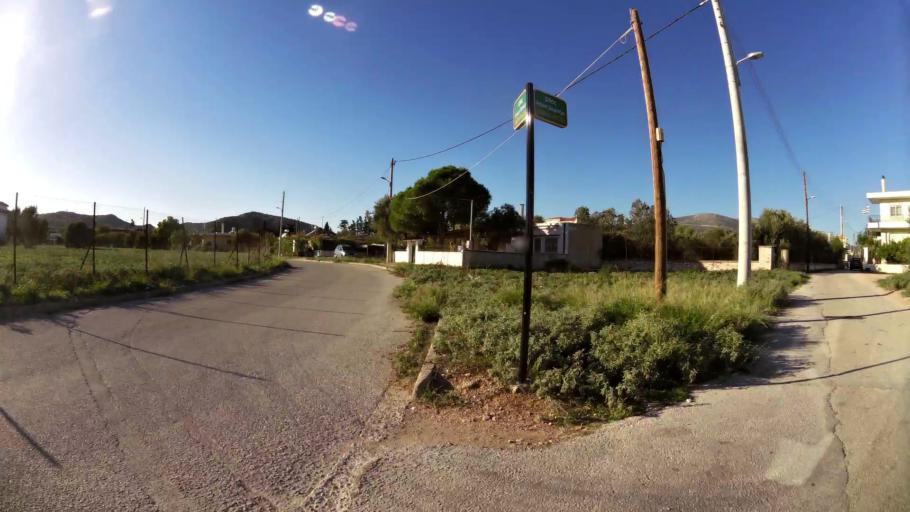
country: GR
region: Attica
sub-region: Nomarchia Anatolikis Attikis
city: Vari
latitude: 37.8264
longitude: 23.8106
